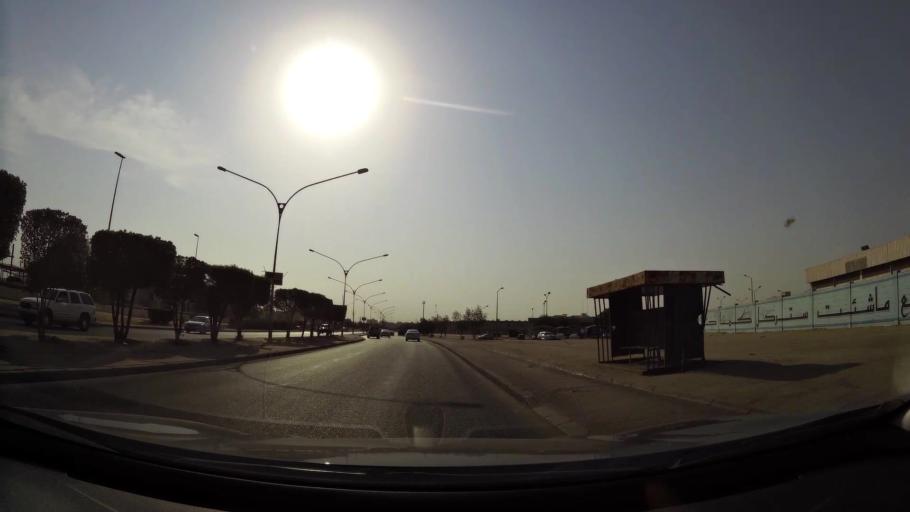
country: KW
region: Mubarak al Kabir
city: Mubarak al Kabir
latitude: 29.1669
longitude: 48.0633
